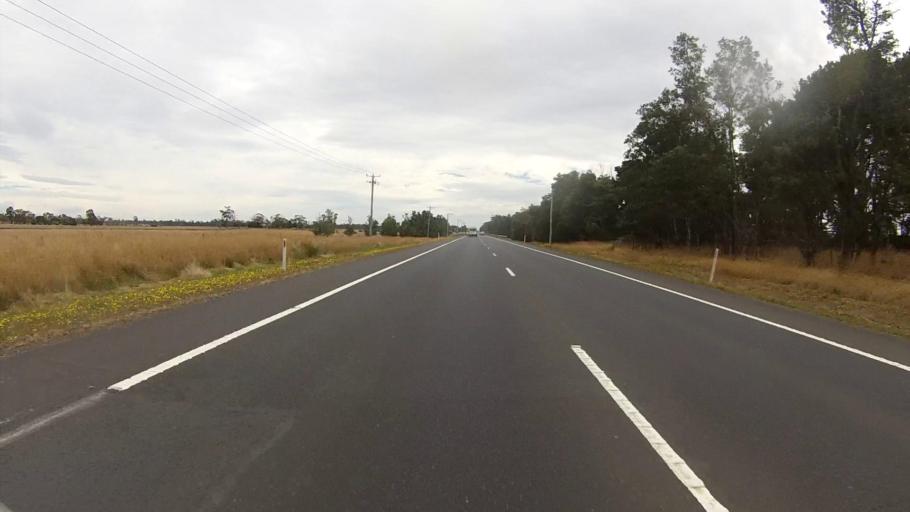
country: AU
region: Tasmania
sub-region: Northern Midlands
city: Evandale
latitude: -41.6934
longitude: 147.2846
